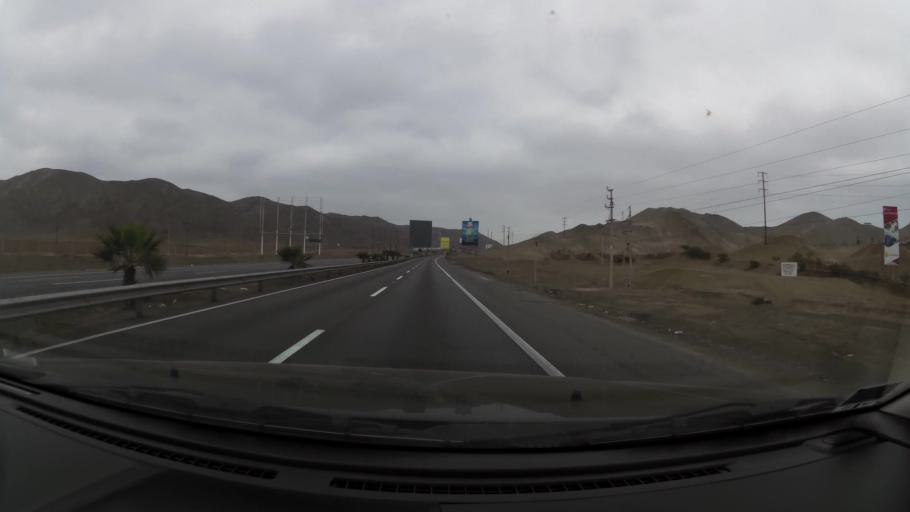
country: PE
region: Lima
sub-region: Lima
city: San Bartolo
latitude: -12.4182
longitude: -76.7547
